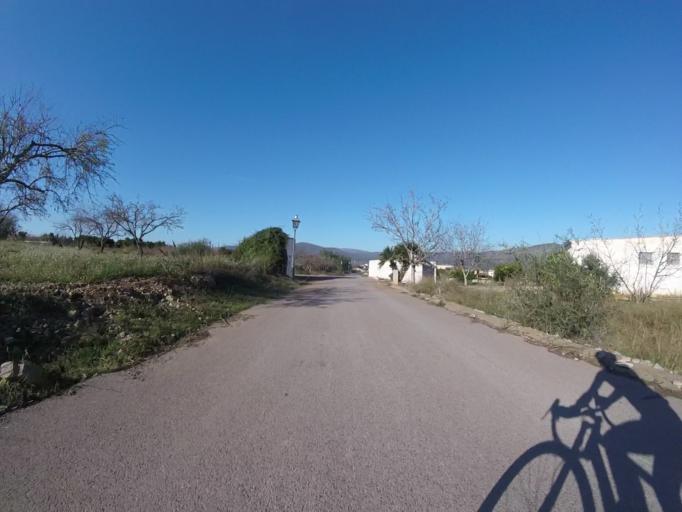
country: ES
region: Valencia
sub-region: Provincia de Castello
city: Santa Magdalena de Pulpis
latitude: 40.3553
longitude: 0.3067
